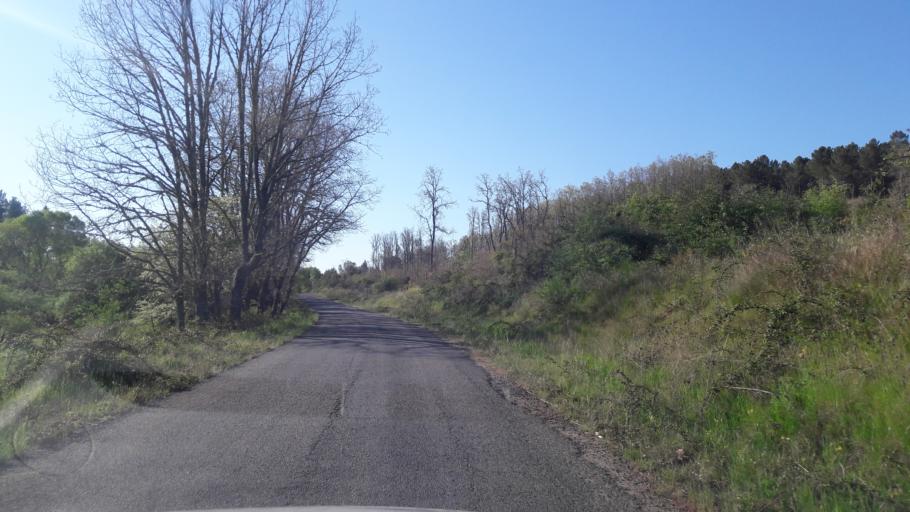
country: ES
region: Castille and Leon
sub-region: Provincia de Salamanca
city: Endrinal
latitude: 40.6033
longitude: -5.8182
